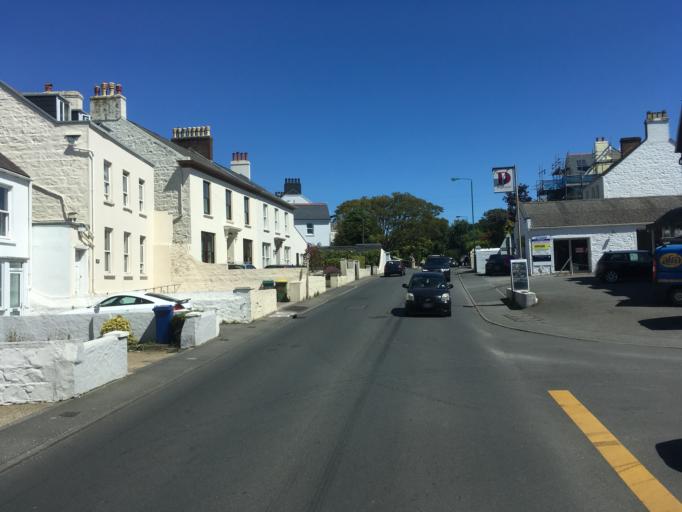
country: GG
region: St Peter Port
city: Saint Peter Port
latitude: 49.4596
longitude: -2.5557
